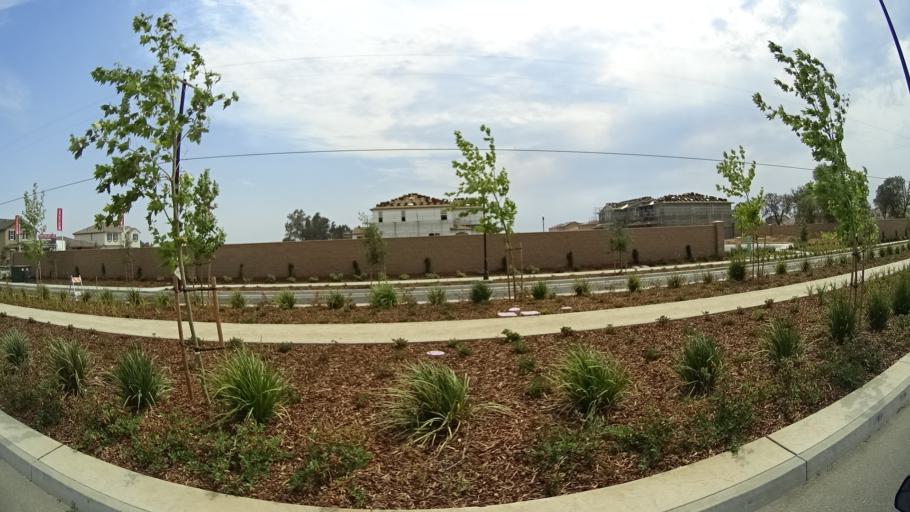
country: US
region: California
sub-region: Sacramento County
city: Laguna
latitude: 38.3908
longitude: -121.4117
